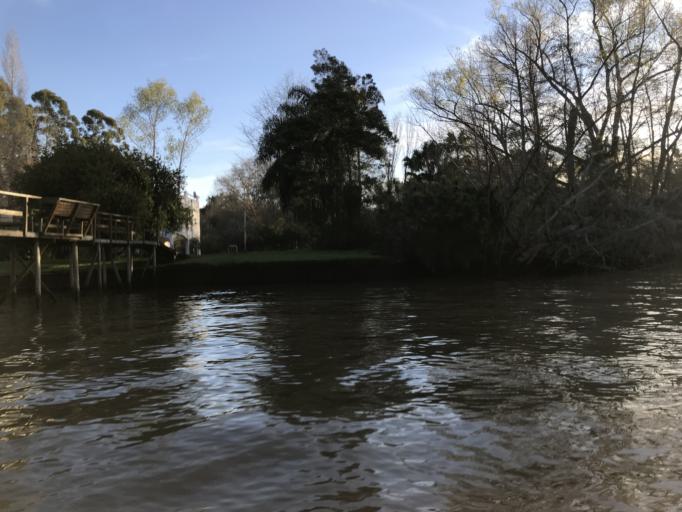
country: AR
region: Buenos Aires
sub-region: Partido de Tigre
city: Tigre
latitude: -34.3799
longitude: -58.5747
